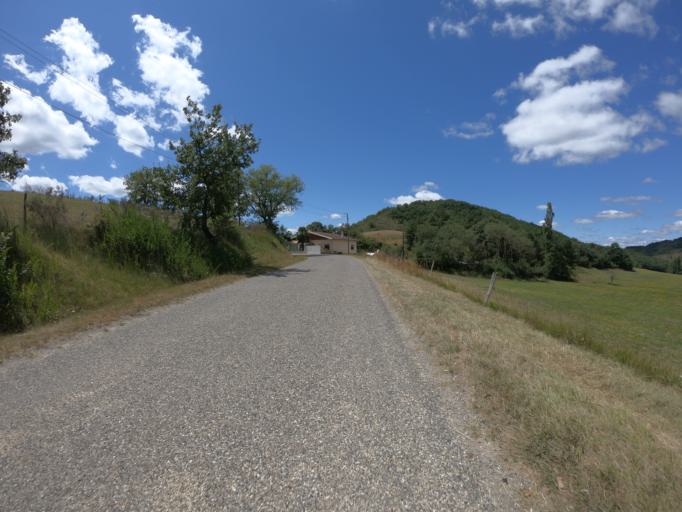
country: FR
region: Midi-Pyrenees
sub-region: Departement de l'Ariege
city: Mirepoix
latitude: 43.0500
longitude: 1.8359
